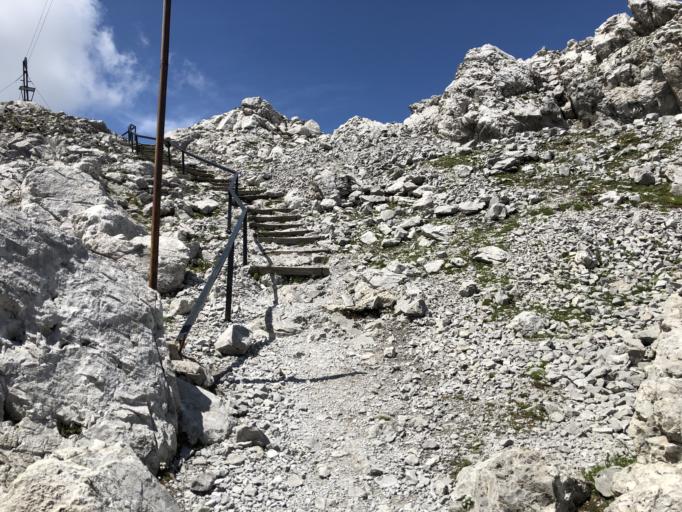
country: AT
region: Tyrol
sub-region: Innsbruck Stadt
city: Innsbruck
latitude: 47.3120
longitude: 11.3819
